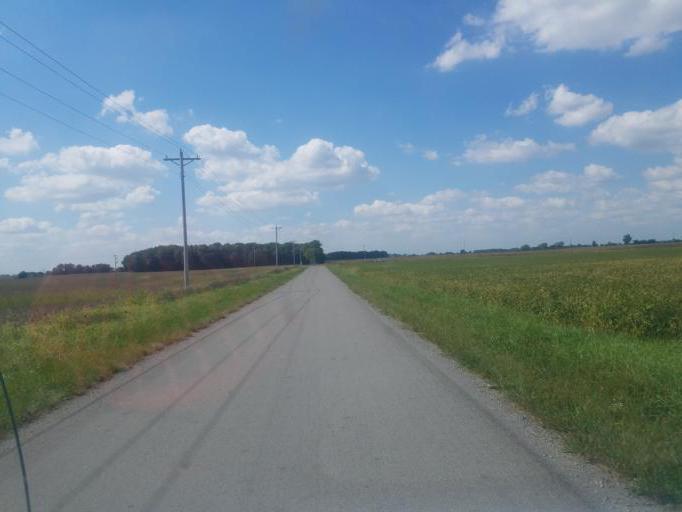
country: US
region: Ohio
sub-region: Hardin County
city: Ada
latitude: 40.6600
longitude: -83.8479
